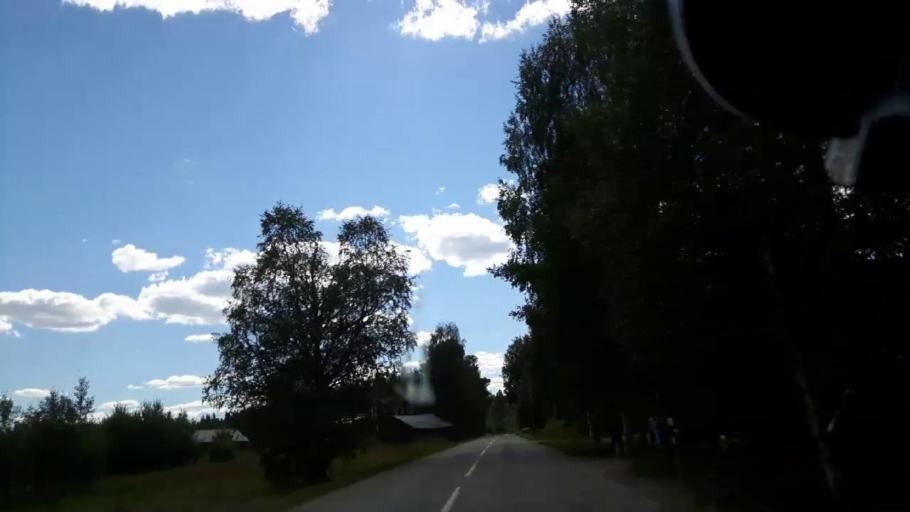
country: SE
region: Jaemtland
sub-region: Ragunda Kommun
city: Hammarstrand
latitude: 62.8974
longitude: 16.2274
